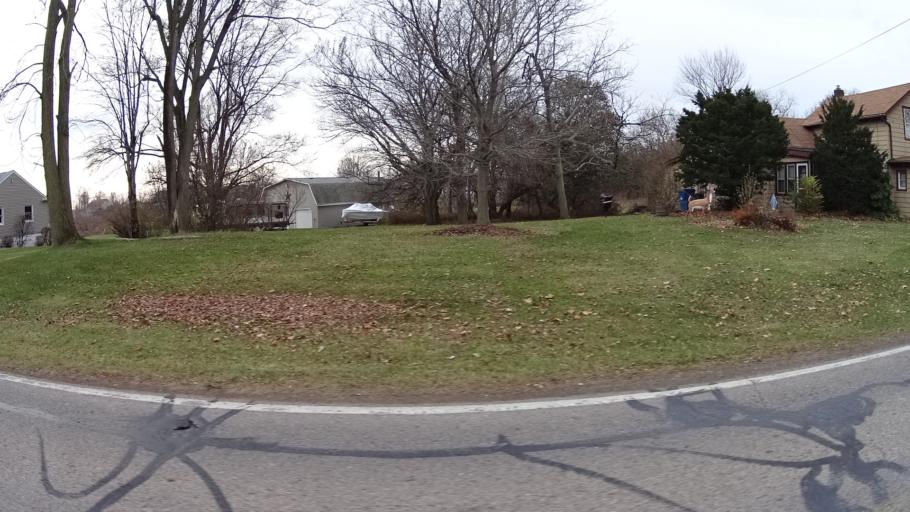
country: US
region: Ohio
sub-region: Lorain County
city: North Ridgeville
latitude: 41.4042
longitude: -82.0332
